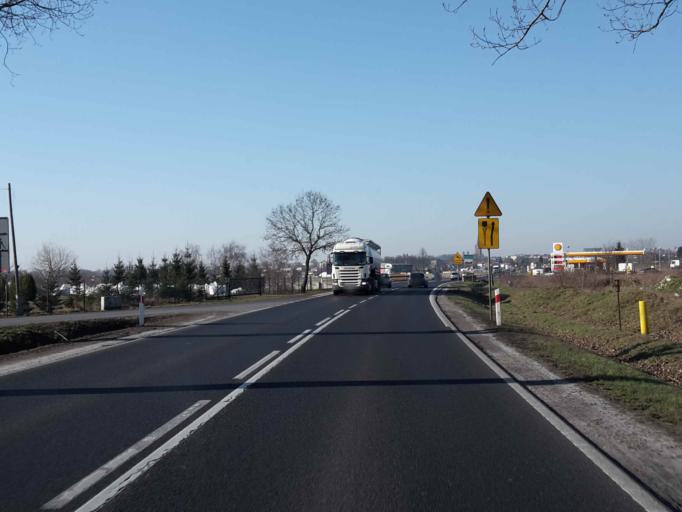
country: PL
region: Kujawsko-Pomorskie
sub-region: Powiat inowroclawski
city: Inowroclaw
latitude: 52.8114
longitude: 18.2835
